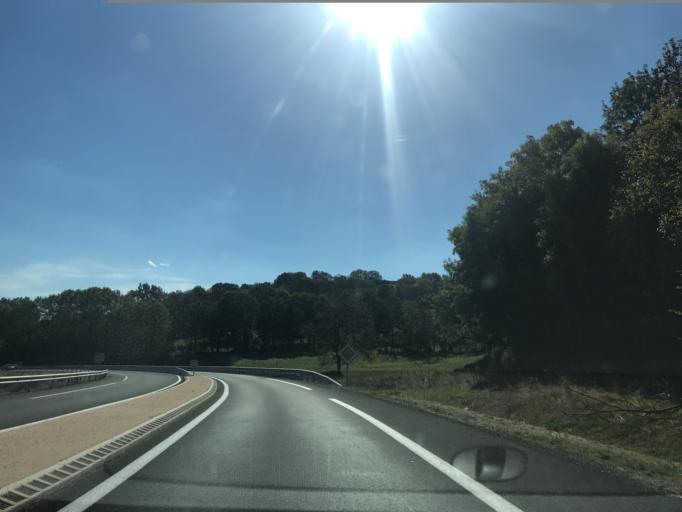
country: FR
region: Auvergne
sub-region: Departement du Puy-de-Dome
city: Gelles
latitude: 45.7346
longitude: 2.8148
